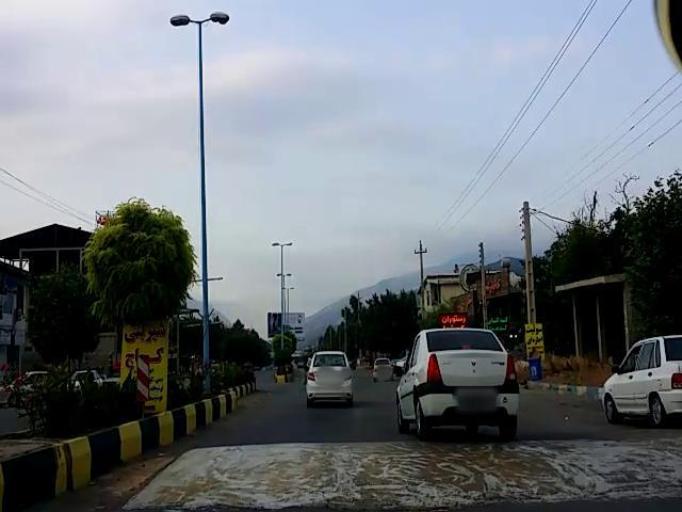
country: IR
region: Mazandaran
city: Chalus
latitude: 36.4446
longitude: 51.2957
